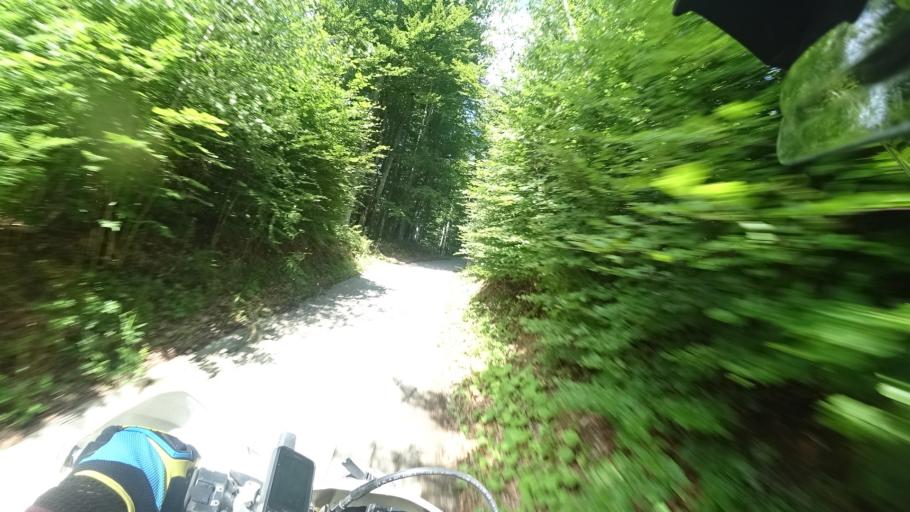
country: SI
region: Osilnica
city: Osilnica
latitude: 45.5151
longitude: 14.6850
